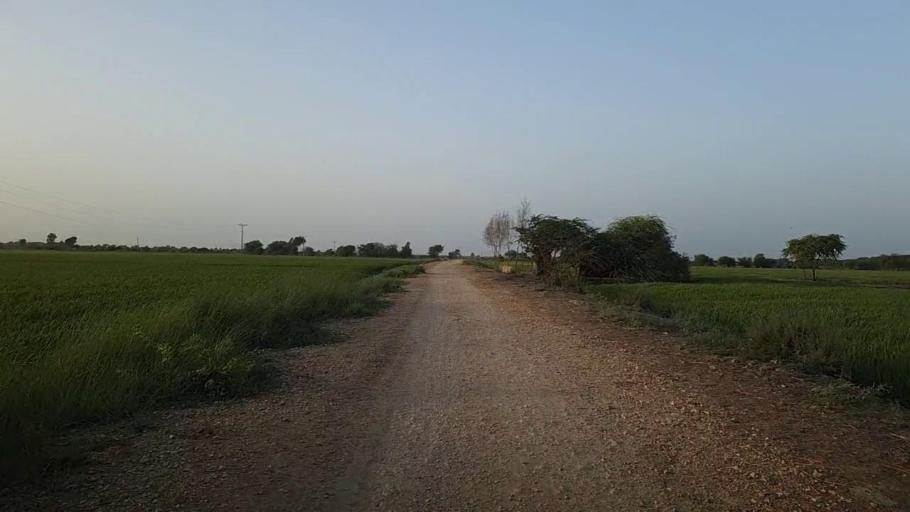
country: PK
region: Sindh
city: Kario
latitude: 24.7217
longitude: 68.4630
